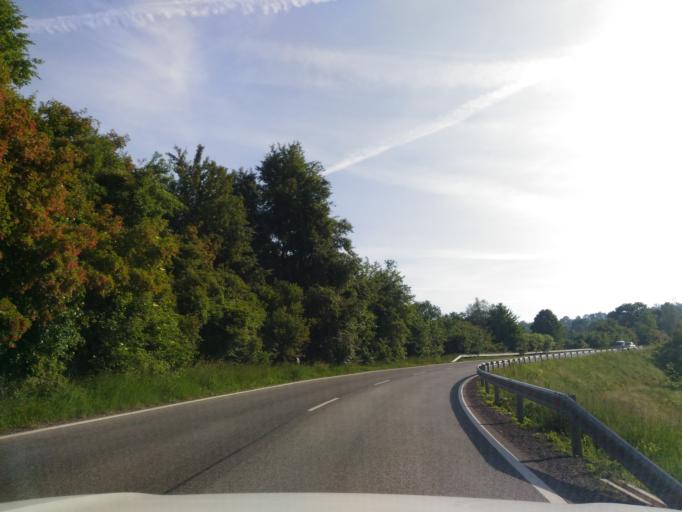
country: HU
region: Baranya
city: Komlo
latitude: 46.1671
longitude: 18.2548
